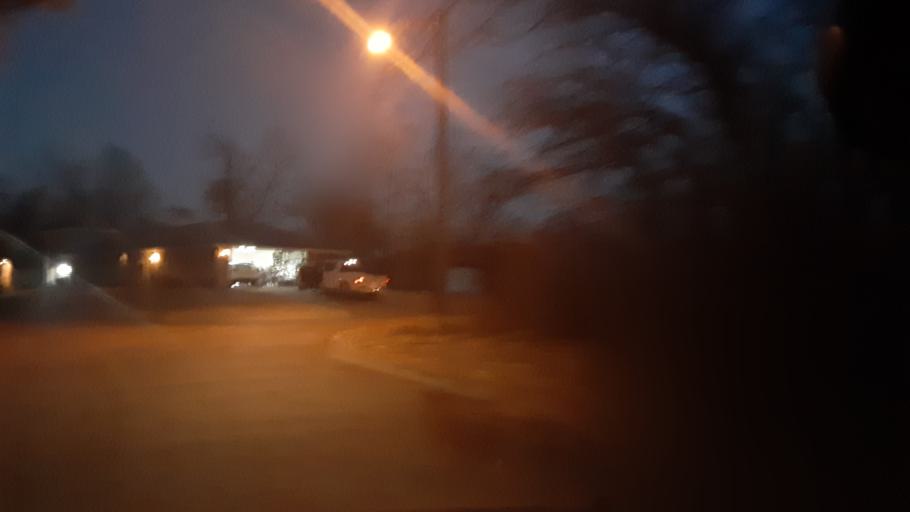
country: US
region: Oklahoma
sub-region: Payne County
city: Stillwater
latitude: 36.1096
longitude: -97.0840
